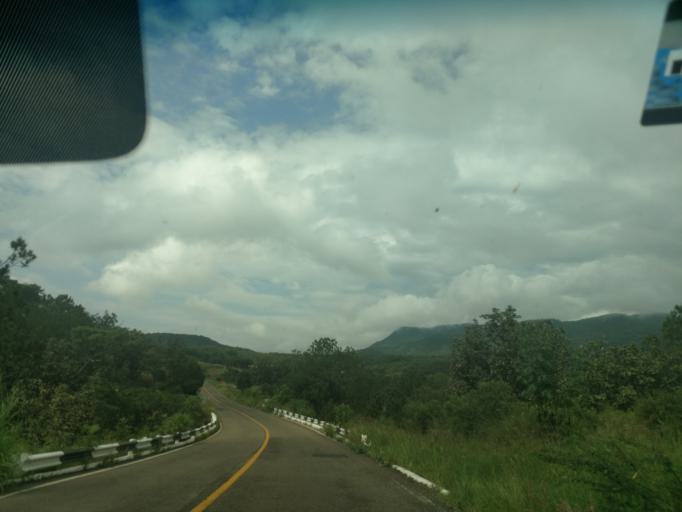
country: MX
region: Jalisco
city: El Salto
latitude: 20.3831
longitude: -104.5409
